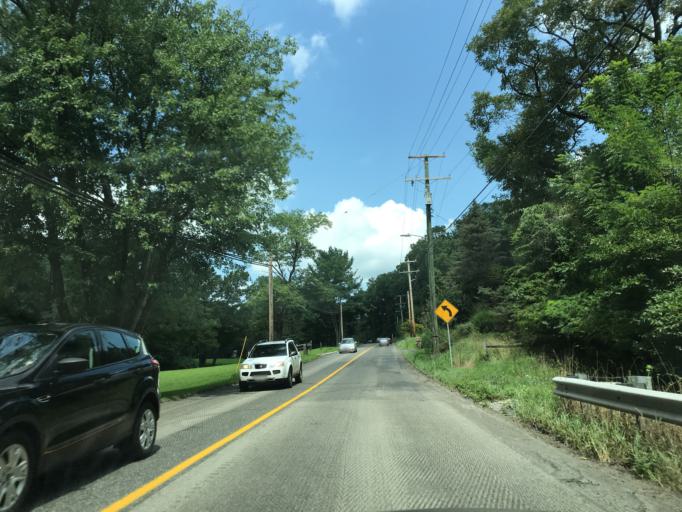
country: US
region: Pennsylvania
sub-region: York County
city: New Freedom
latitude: 39.6398
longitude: -76.6891
